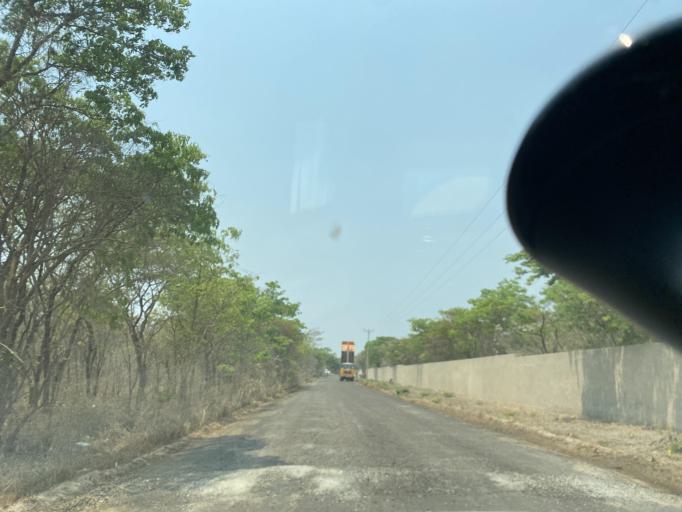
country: ZM
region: Lusaka
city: Lusaka
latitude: -15.5097
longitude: 28.4458
